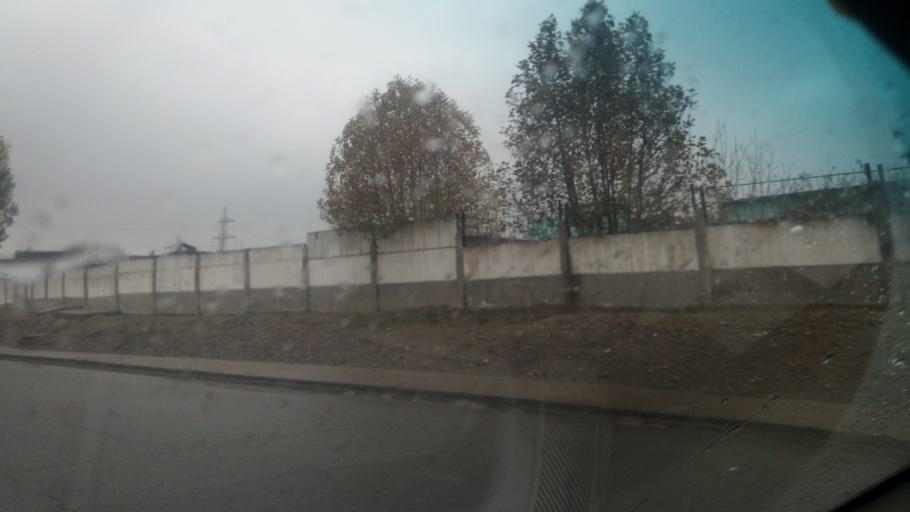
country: UZ
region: Toshkent Shahri
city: Bektemir
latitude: 41.2465
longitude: 69.3476
